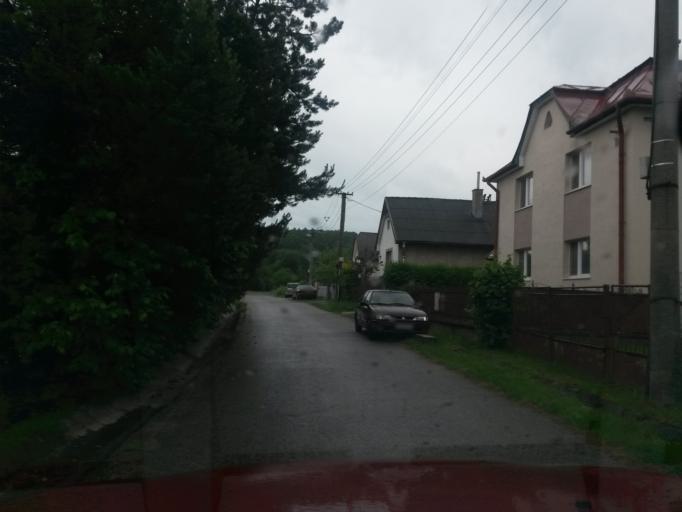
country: SK
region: Kosicky
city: Kosice
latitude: 48.7038
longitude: 21.1797
